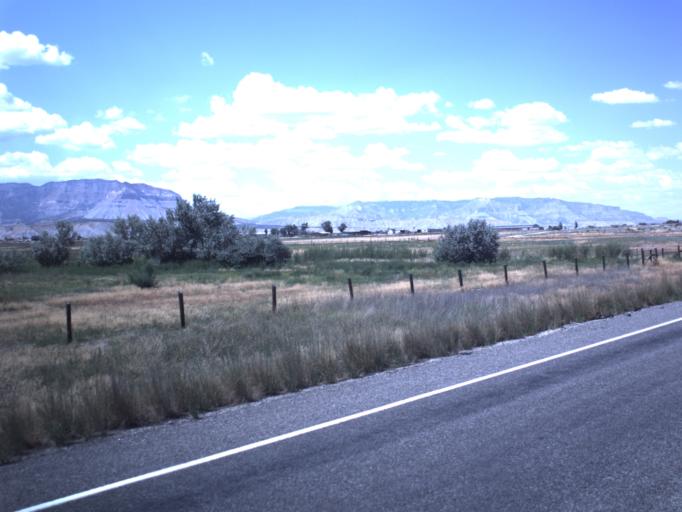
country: US
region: Utah
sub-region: Emery County
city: Castle Dale
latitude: 39.2346
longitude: -110.9924
